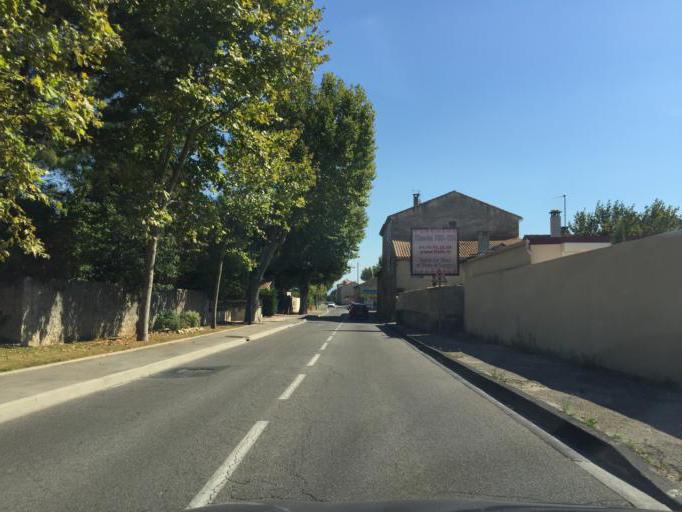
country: FR
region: Provence-Alpes-Cote d'Azur
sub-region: Departement du Vaucluse
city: Saint-Saturnin-les-Avignon
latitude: 43.9583
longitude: 4.9364
